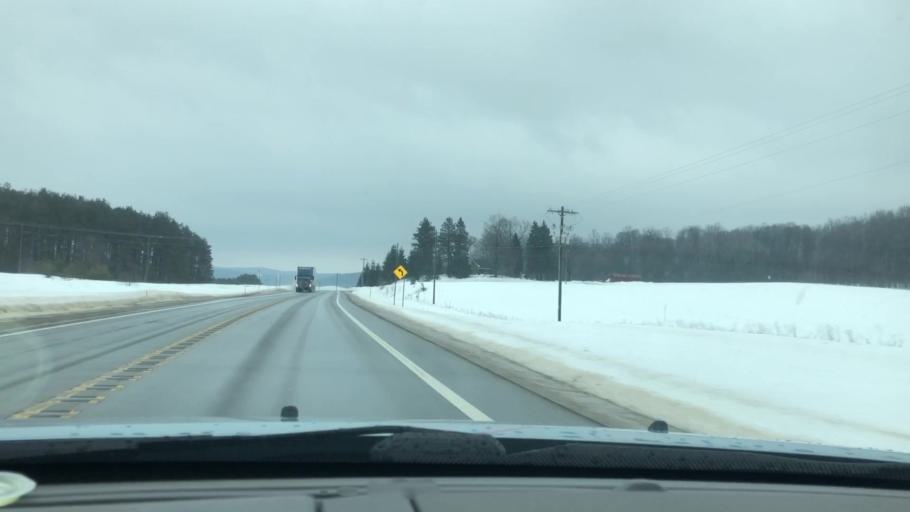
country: US
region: Michigan
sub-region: Charlevoix County
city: Boyne City
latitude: 45.0960
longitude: -84.9816
